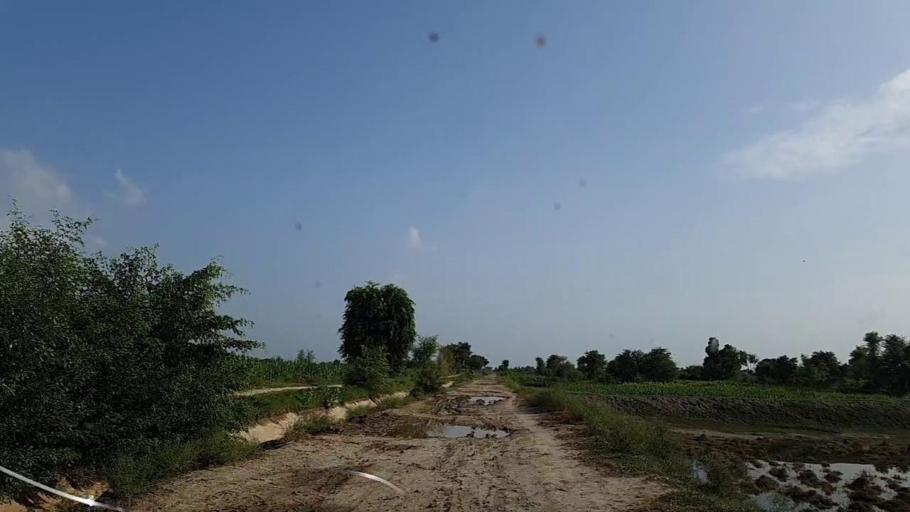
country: PK
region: Sindh
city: Bhiria
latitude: 26.8594
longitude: 68.2511
